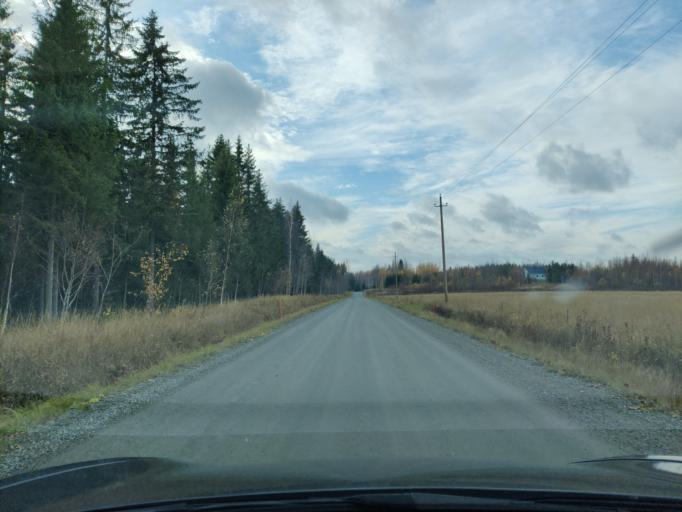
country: FI
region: Northern Savo
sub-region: Kuopio
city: Siilinjaervi
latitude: 63.1213
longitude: 27.5488
